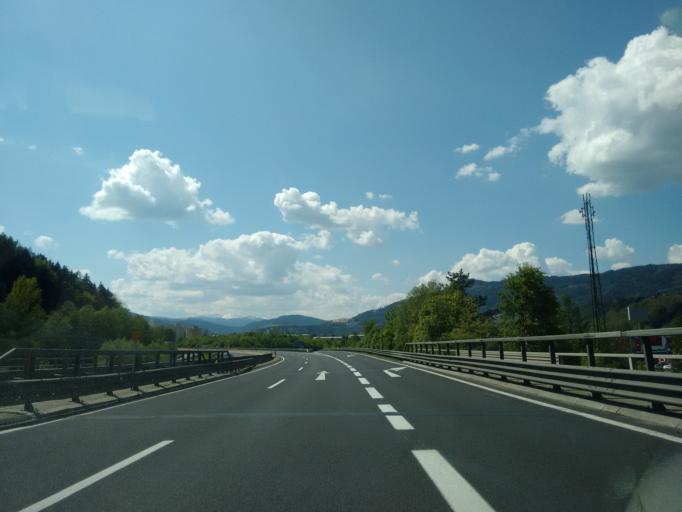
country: AT
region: Styria
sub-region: Politischer Bezirk Leoben
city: Proleb
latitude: 47.3834
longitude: 15.1287
